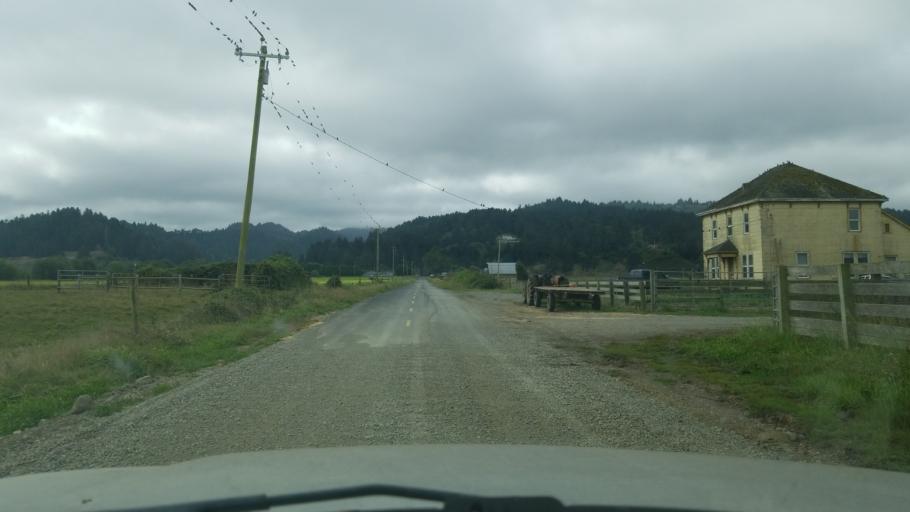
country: US
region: California
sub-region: Humboldt County
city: Ferndale
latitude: 40.5895
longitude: -124.2840
